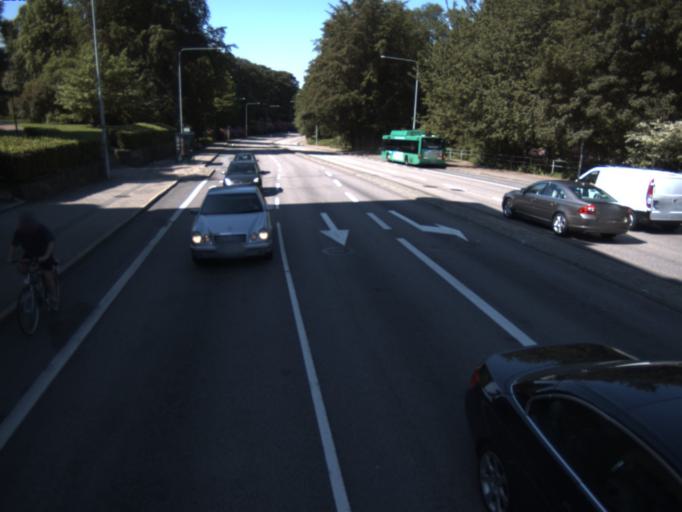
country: SE
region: Skane
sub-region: Helsingborg
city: Helsingborg
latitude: 56.0540
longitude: 12.6965
